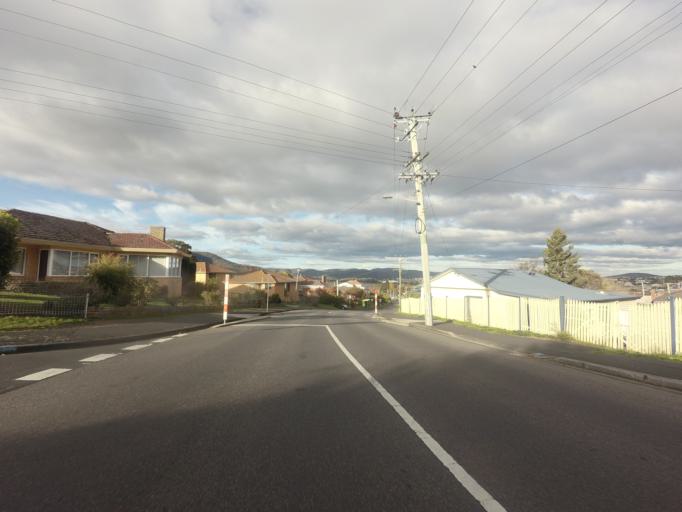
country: AU
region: Tasmania
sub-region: Glenorchy
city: Berriedale
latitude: -42.8227
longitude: 147.2598
